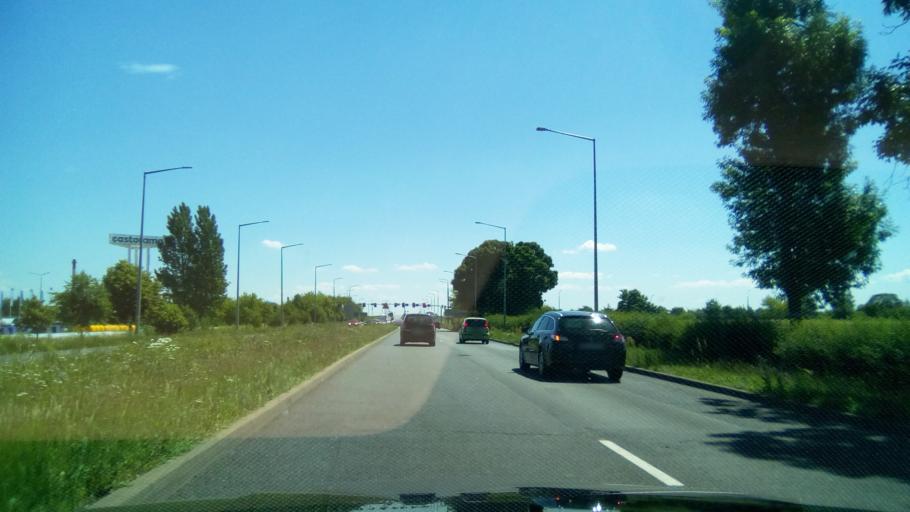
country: PL
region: Masovian Voivodeship
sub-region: Radom
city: Radom
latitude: 51.4218
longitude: 21.1768
